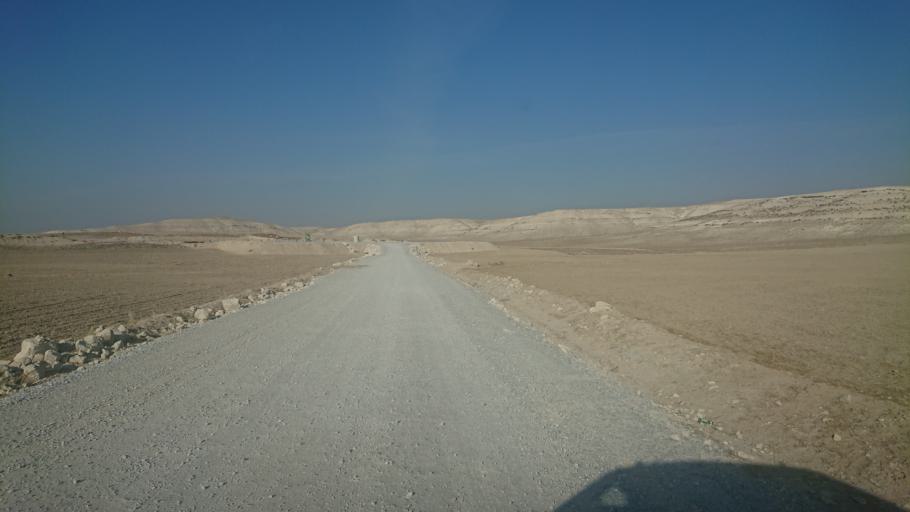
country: TR
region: Aksaray
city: Sultanhani
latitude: 38.0840
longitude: 33.6209
